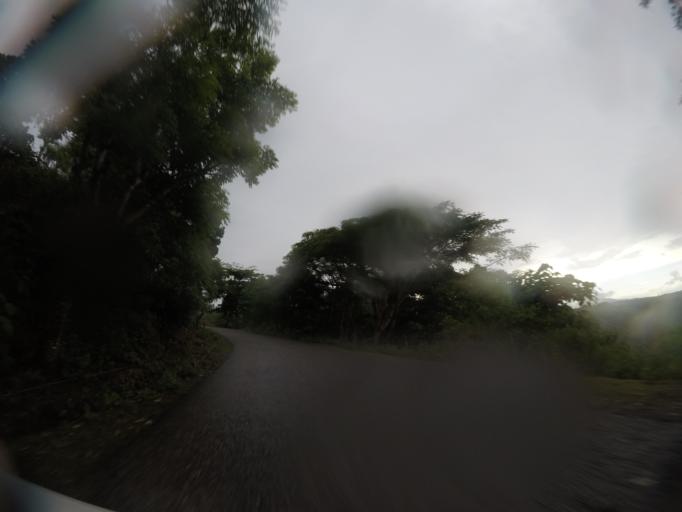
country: TL
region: Bobonaro
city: Maliana
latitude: -8.9624
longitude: 125.0311
